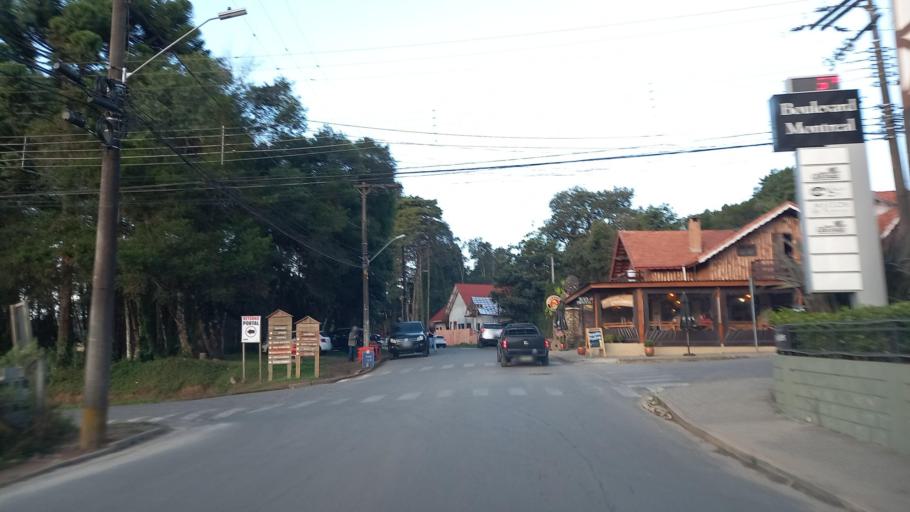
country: BR
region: Minas Gerais
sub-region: Camanducaia
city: Camanducaia
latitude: -22.8597
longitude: -46.0302
